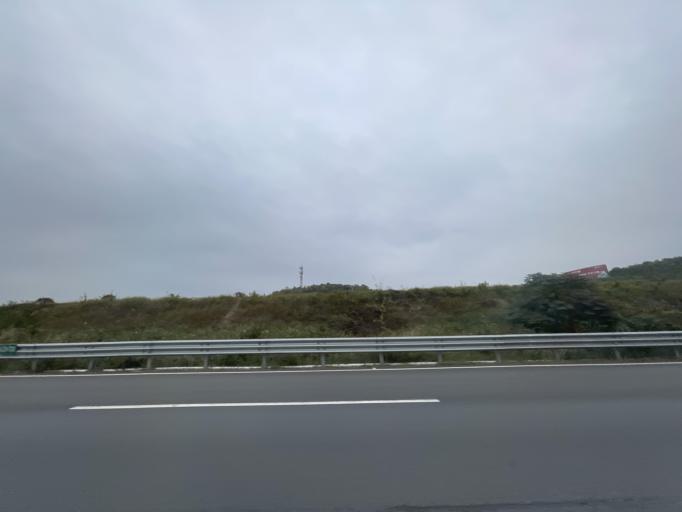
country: CN
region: Guangdong
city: Xinwan
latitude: 22.8075
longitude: 113.6369
